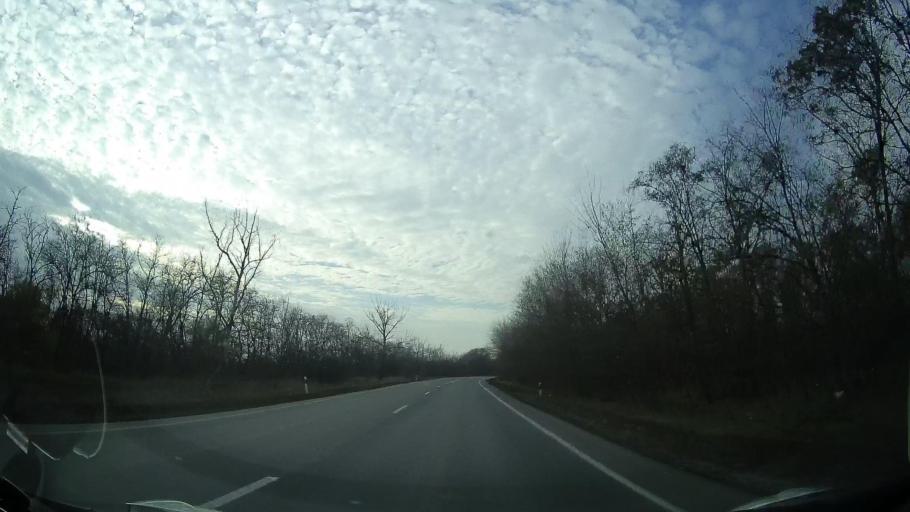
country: RU
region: Rostov
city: Bagayevskaya
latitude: 47.0962
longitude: 40.2851
